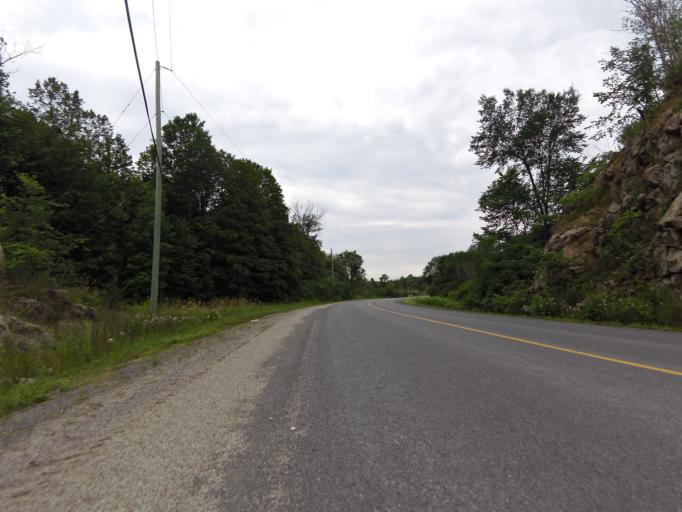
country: CA
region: Ontario
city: Kingston
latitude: 44.5653
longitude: -76.6295
